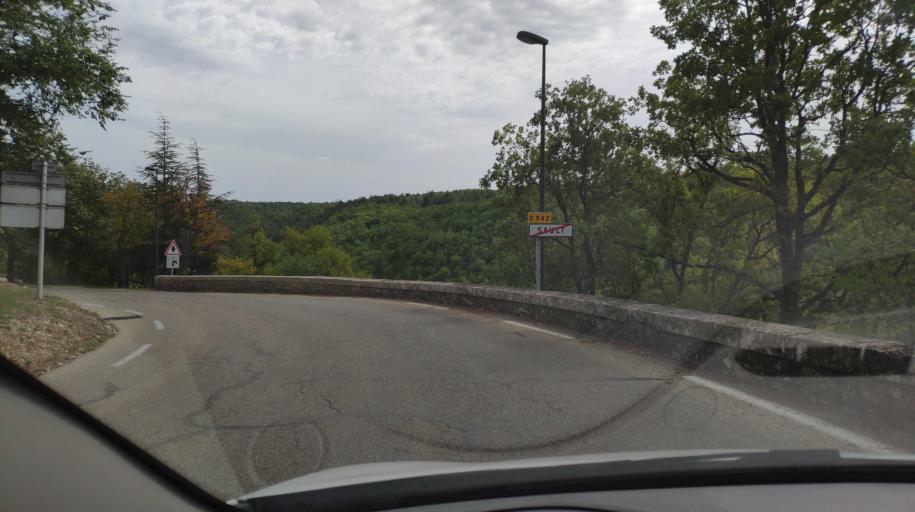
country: FR
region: Provence-Alpes-Cote d'Azur
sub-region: Departement du Vaucluse
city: Sault
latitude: 44.0889
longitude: 5.4115
